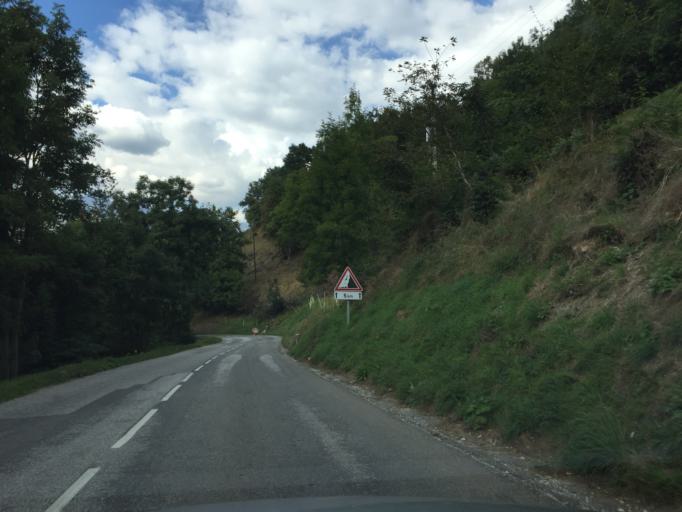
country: FR
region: Rhone-Alpes
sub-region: Departement de la Savoie
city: Belle-Plagne
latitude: 45.5473
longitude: 6.7534
